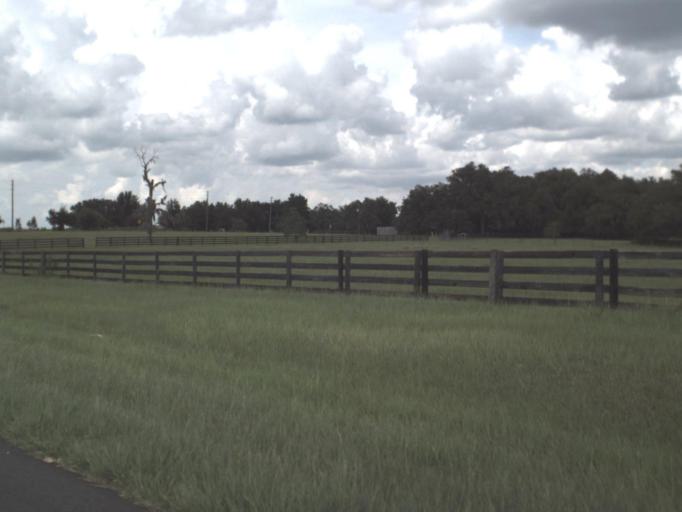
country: US
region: Florida
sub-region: Citrus County
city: Floral City
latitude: 28.7092
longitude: -82.3120
